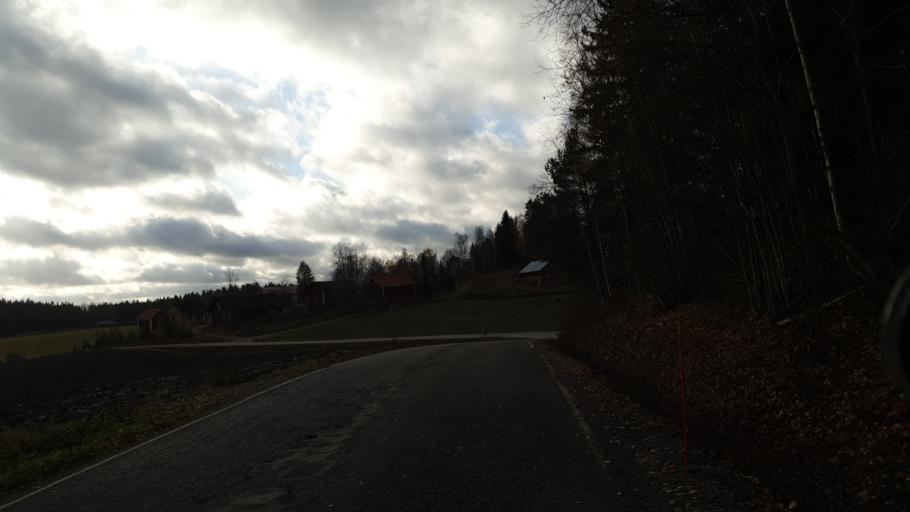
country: FI
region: Uusimaa
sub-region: Helsinki
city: Siuntio
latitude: 60.2491
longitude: 24.2990
